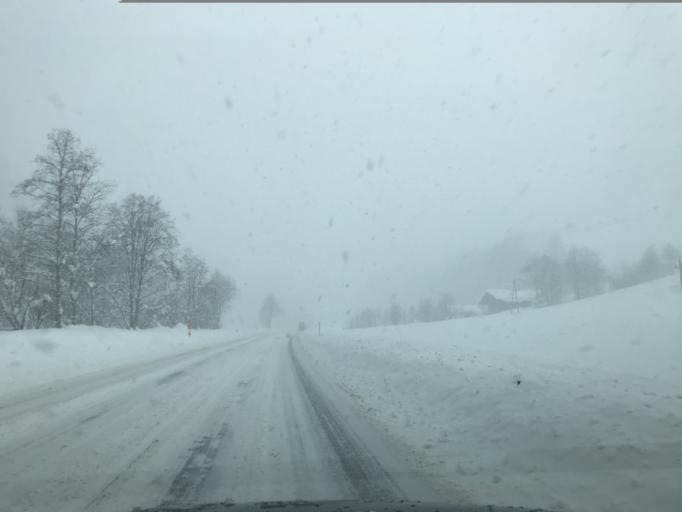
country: AT
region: Salzburg
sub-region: Politischer Bezirk Zell am See
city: Viehhofen
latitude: 47.3661
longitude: 12.7131
